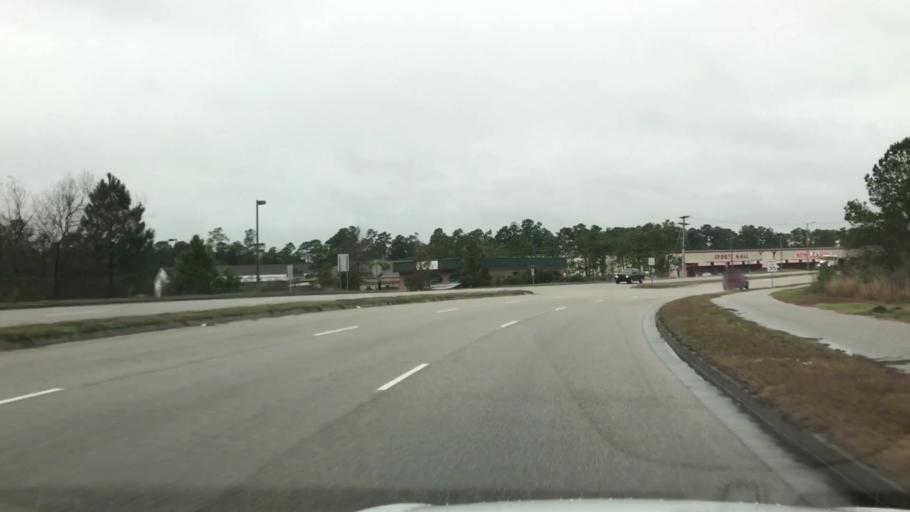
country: US
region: South Carolina
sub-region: Horry County
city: Forestbrook
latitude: 33.7090
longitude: -78.9400
